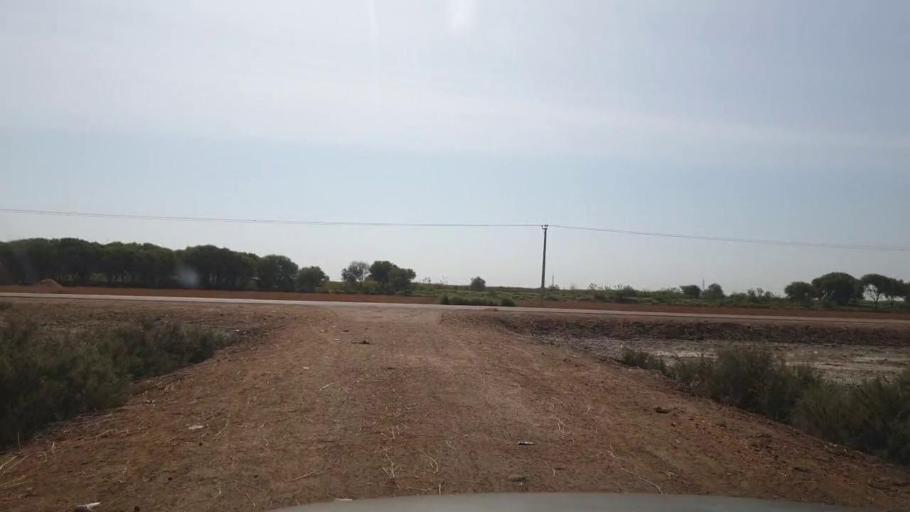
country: PK
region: Sindh
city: Tando Muhammad Khan
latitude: 25.1313
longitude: 68.4192
